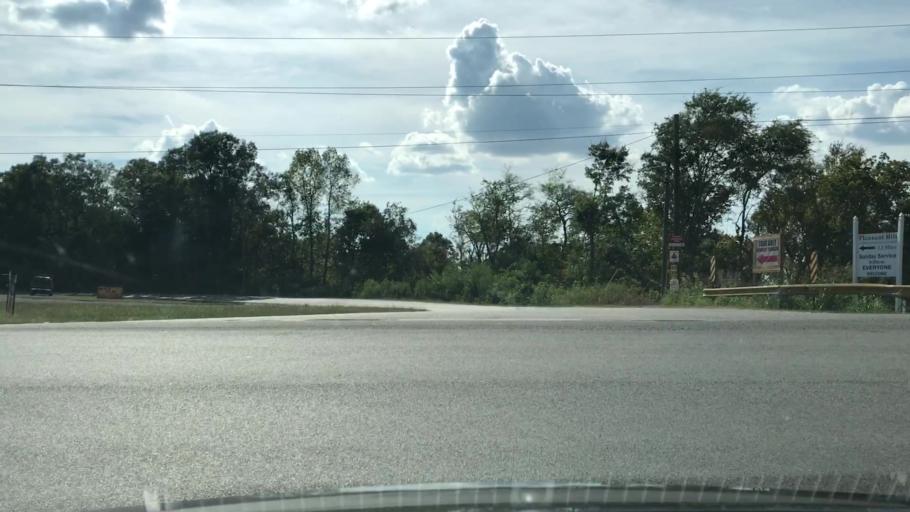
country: US
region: Alabama
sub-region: Limestone County
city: Ardmore
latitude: 35.0157
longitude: -86.8810
